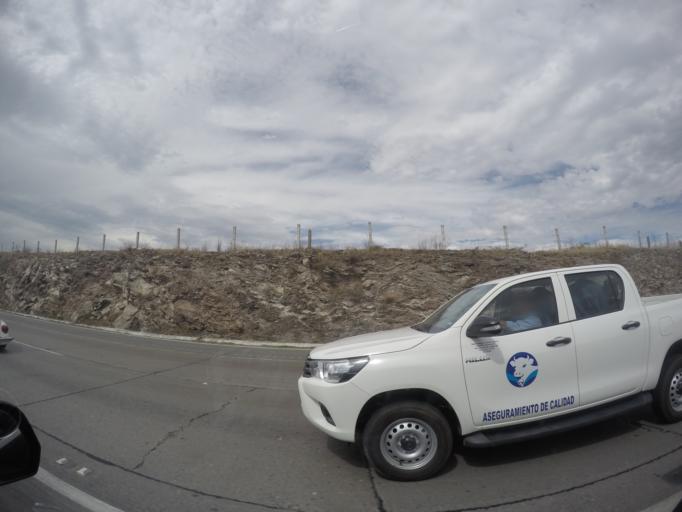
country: MX
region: Queretaro
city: San Juan del Rio
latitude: 20.3632
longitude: -99.9736
